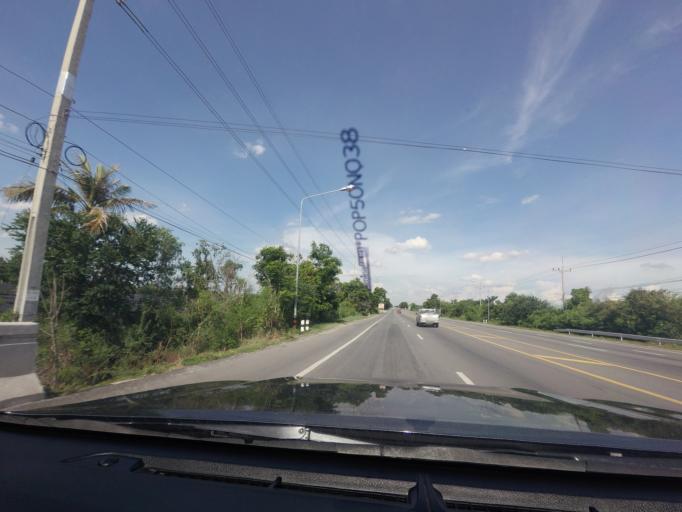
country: TH
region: Phra Nakhon Si Ayutthaya
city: Lat Bua Luang
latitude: 14.1580
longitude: 100.1740
